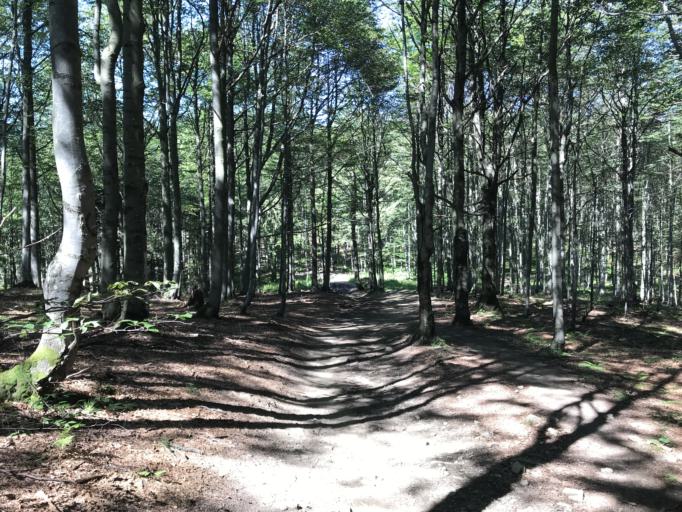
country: PL
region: Lesser Poland Voivodeship
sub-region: Powiat nowosadecki
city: Labowa
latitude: 49.4799
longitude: 20.8029
